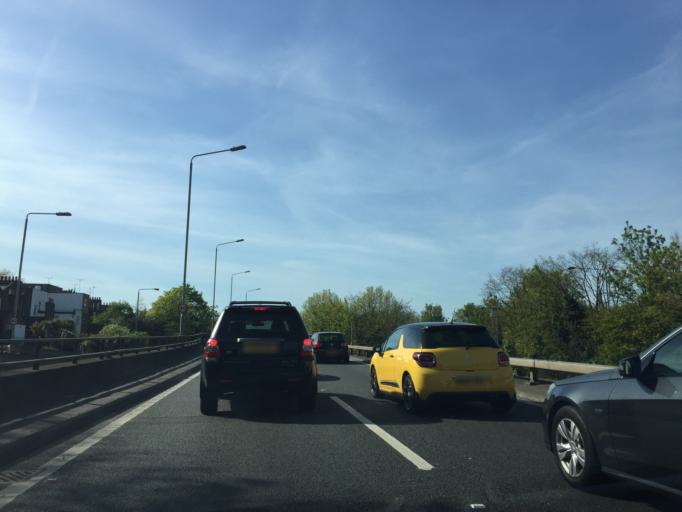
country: GB
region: England
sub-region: Greater London
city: Hackney
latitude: 51.5439
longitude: -0.0303
